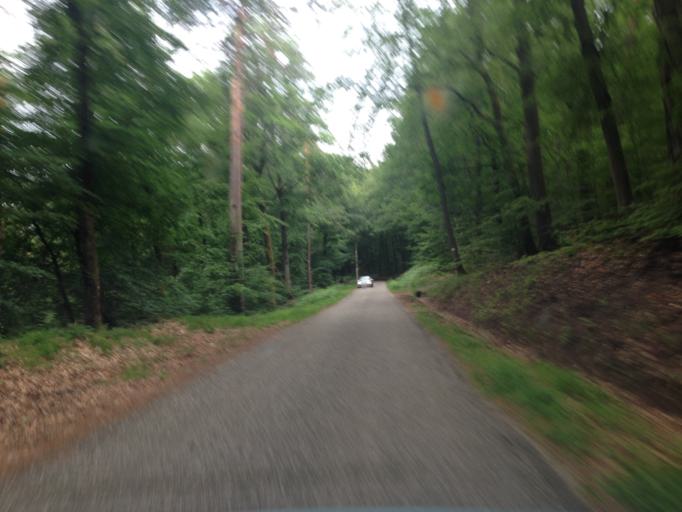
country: FR
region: Alsace
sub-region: Departement du Bas-Rhin
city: Neuwiller-les-Saverne
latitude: 48.8471
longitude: 7.3810
